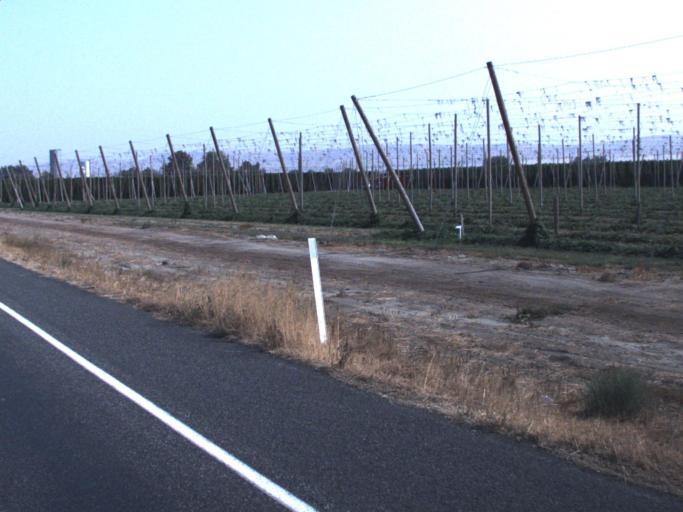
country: US
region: Washington
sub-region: Yakima County
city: Mabton
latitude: 46.2148
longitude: -120.0125
